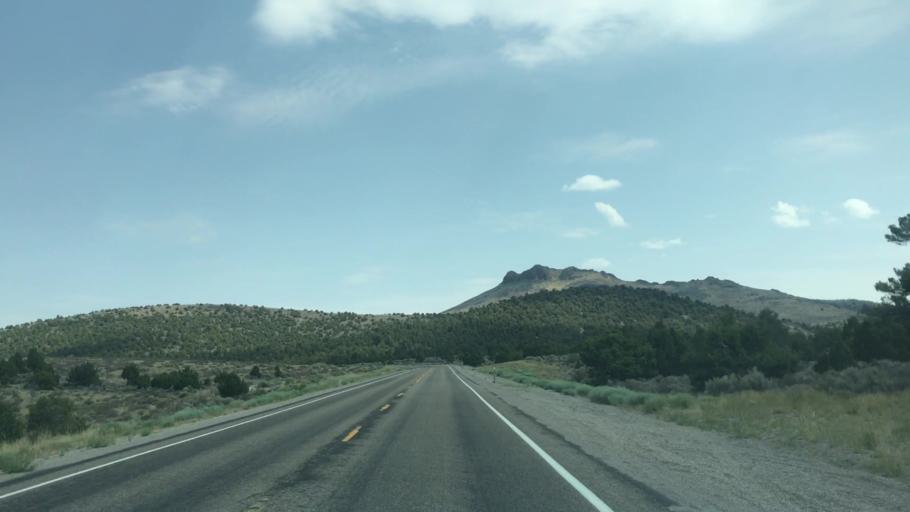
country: US
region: Nevada
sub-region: White Pine County
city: Ely
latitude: 39.4070
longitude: -115.0797
